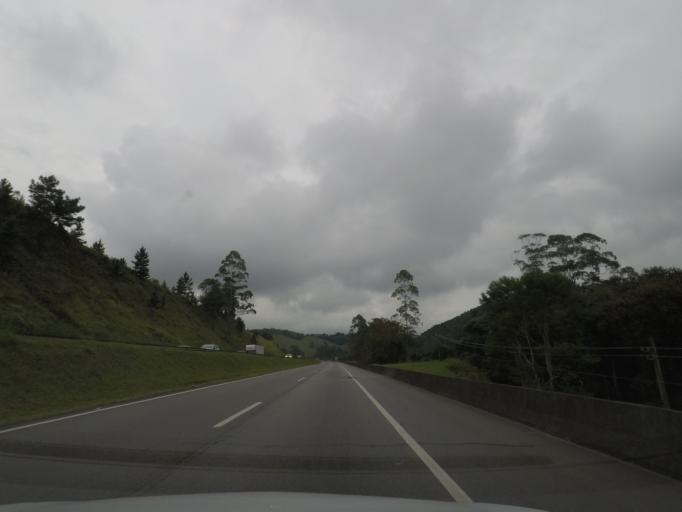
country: BR
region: Sao Paulo
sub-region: Juquitiba
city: Juquitiba
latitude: -23.9967
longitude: -47.1488
